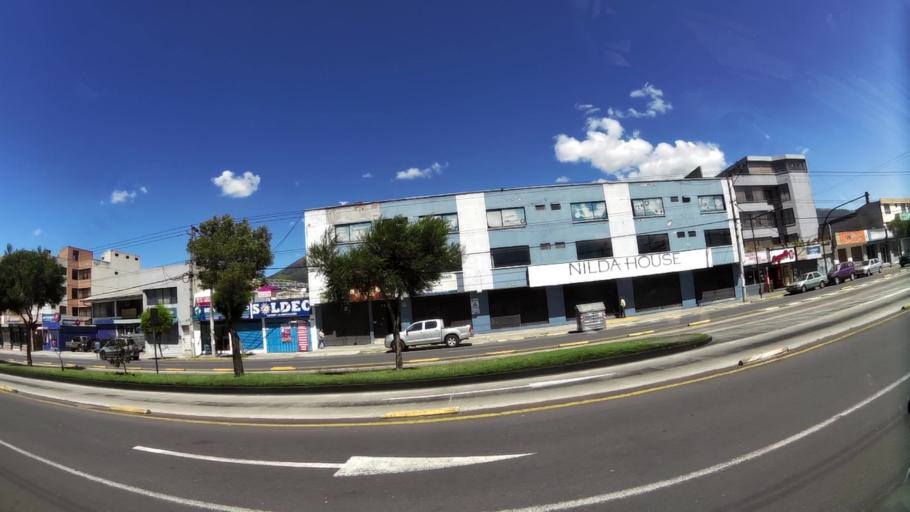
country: EC
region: Pichincha
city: Quito
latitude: -0.1547
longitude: -78.4888
